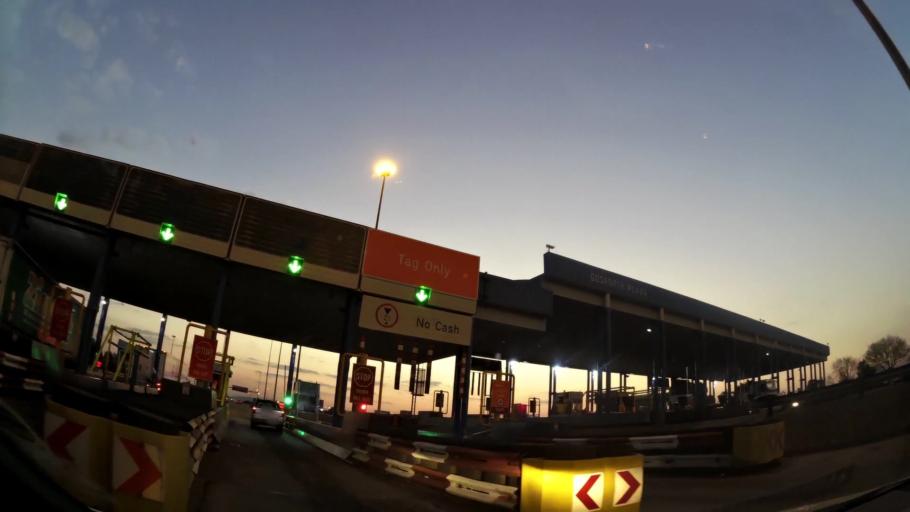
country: ZA
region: Gauteng
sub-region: Ekurhuleni Metropolitan Municipality
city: Germiston
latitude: -26.2484
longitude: 28.1585
